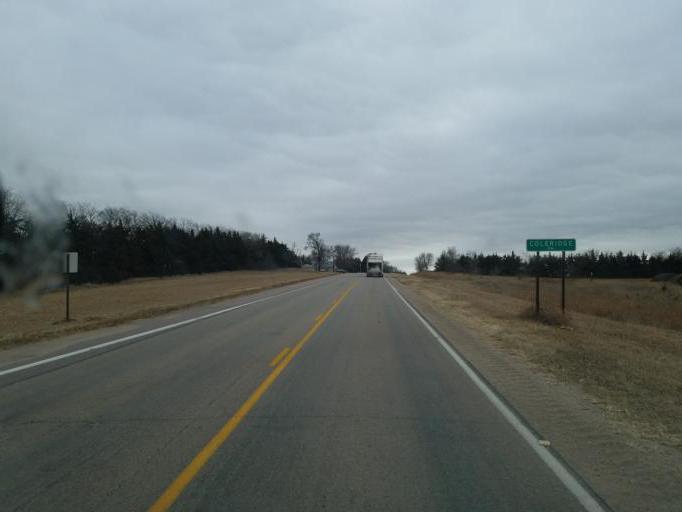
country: US
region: Nebraska
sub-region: Cedar County
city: Hartington
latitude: 42.5099
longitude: -97.2121
